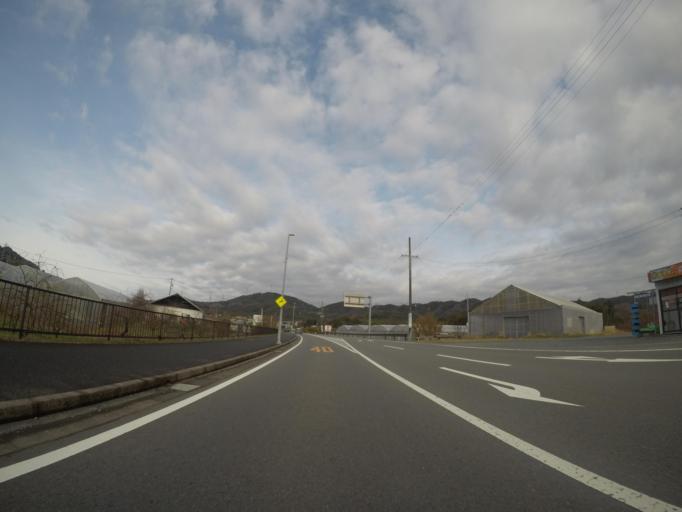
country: JP
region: Shizuoka
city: Hamakita
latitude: 34.8270
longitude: 137.7278
